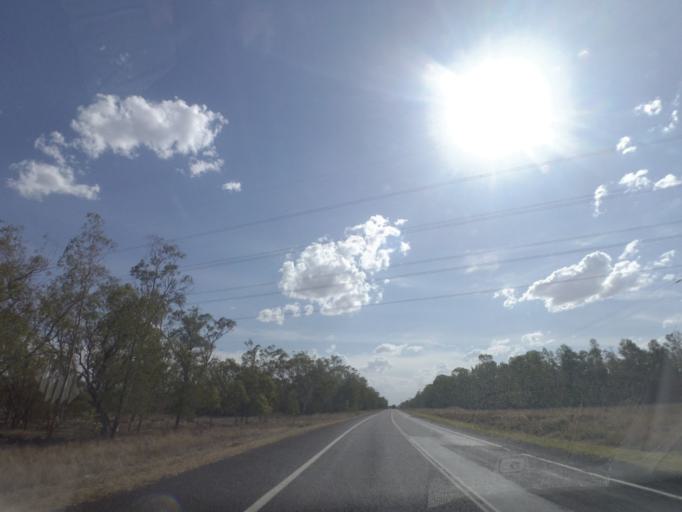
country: AU
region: New South Wales
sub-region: Moree Plains
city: Boggabilla
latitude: -28.5441
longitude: 150.8819
